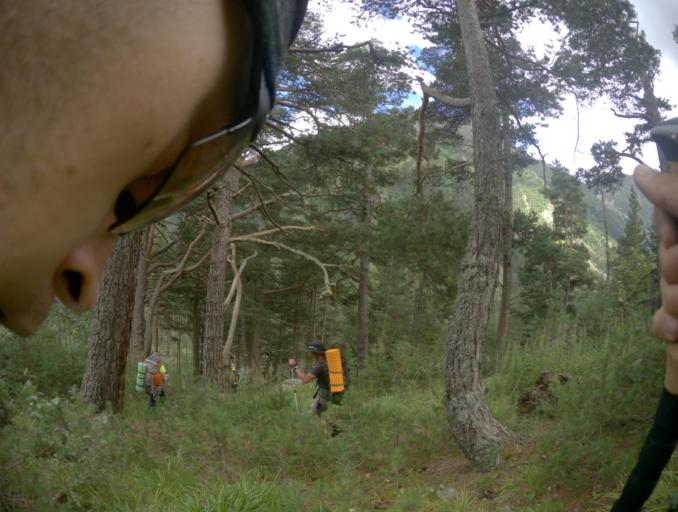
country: RU
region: Karachayevo-Cherkesiya
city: Uchkulan
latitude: 43.3490
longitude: 42.1520
